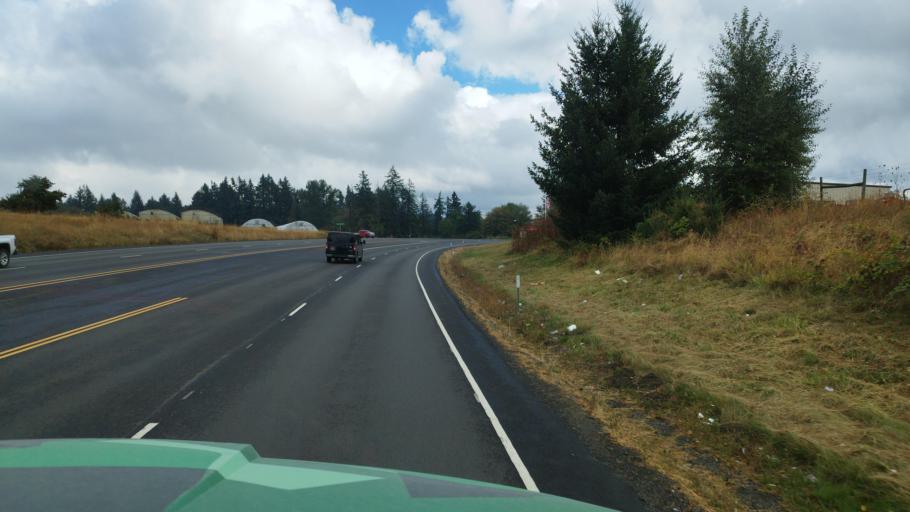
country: US
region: Oregon
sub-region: Yamhill County
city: Lafayette
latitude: 45.2393
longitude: -123.1471
